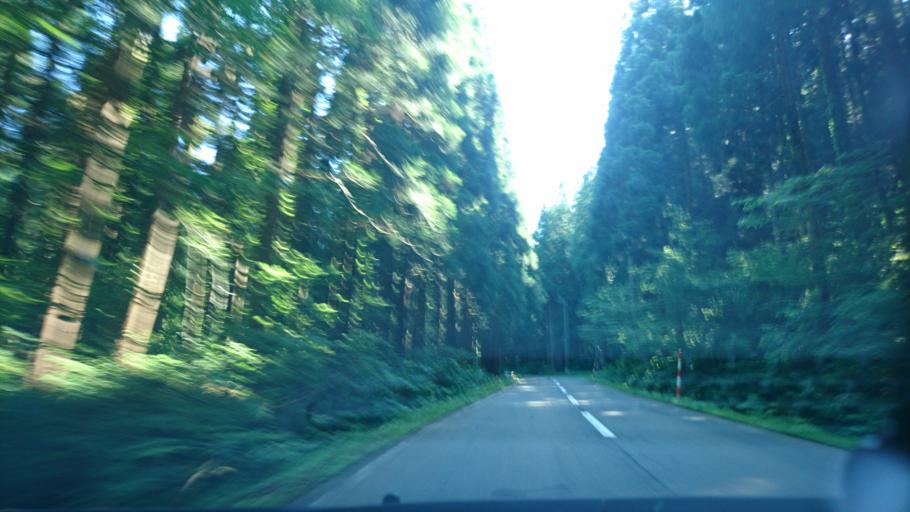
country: JP
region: Akita
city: Kakunodatemachi
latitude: 39.7092
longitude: 140.6079
